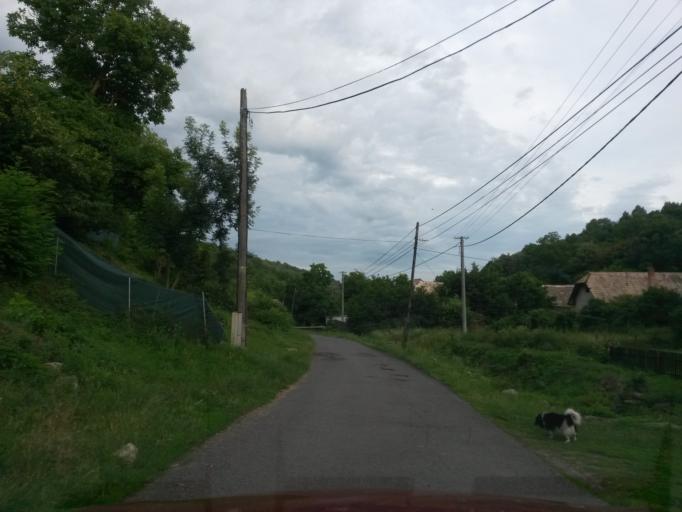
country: SK
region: Banskobystricky
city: Velky Krtis
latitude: 48.3186
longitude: 19.4559
